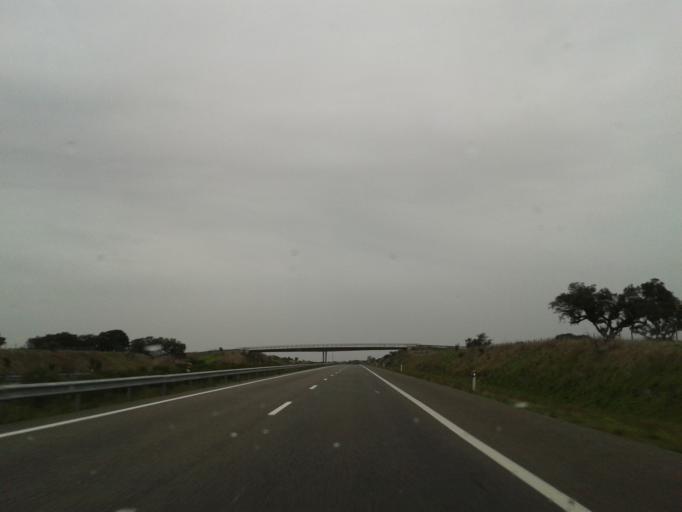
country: PT
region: Beja
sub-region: Ourique
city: Ourique
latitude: 37.6035
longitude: -8.1702
